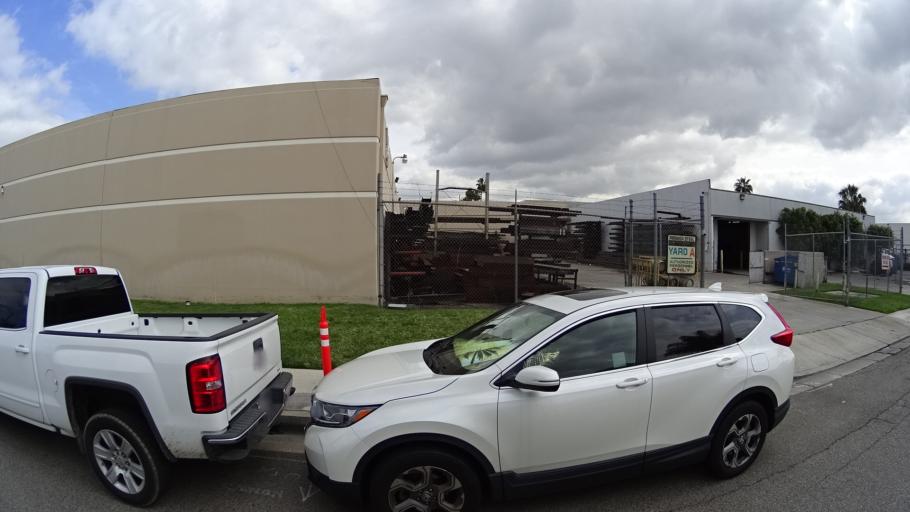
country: US
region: California
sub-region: Orange County
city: Buena Park
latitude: 33.8538
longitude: -117.9797
